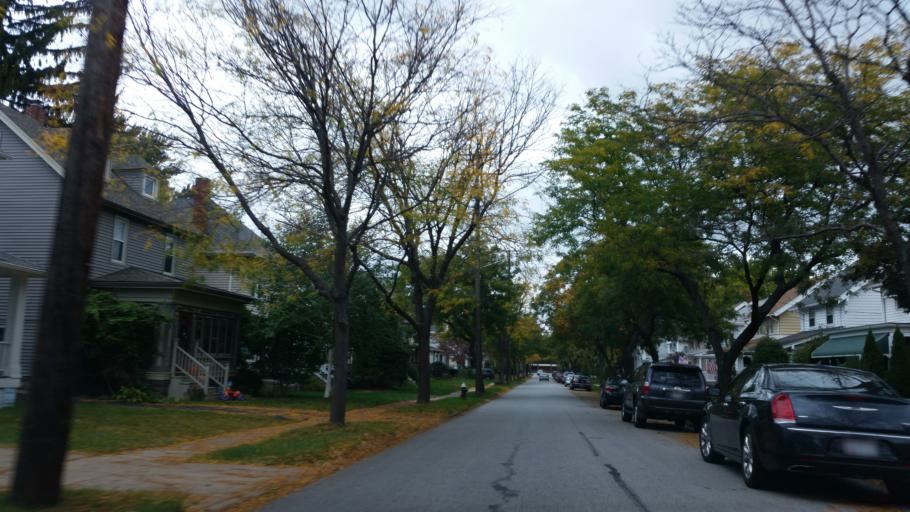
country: US
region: Ohio
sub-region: Cuyahoga County
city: Lakewood
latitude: 41.4829
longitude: -81.8167
